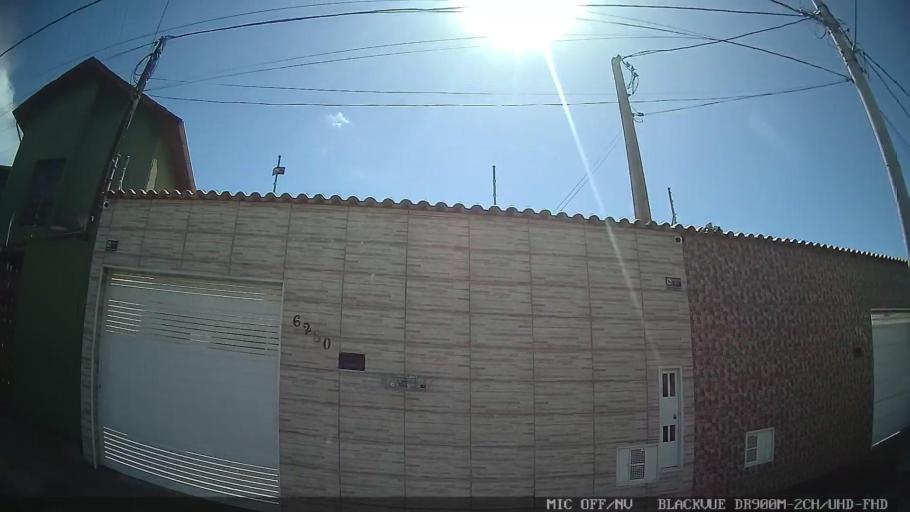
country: BR
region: Sao Paulo
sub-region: Itanhaem
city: Itanhaem
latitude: -24.2365
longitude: -46.8755
